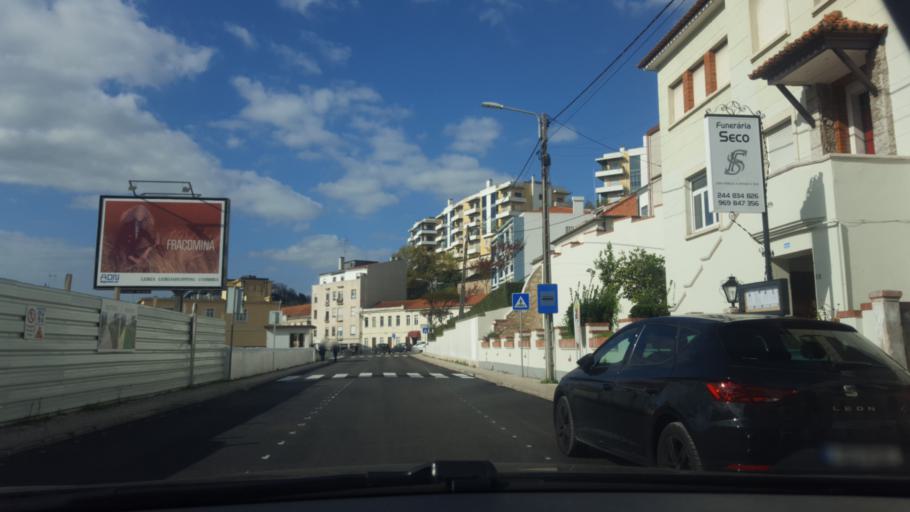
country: PT
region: Leiria
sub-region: Leiria
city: Leiria
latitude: 39.7425
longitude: -8.8017
